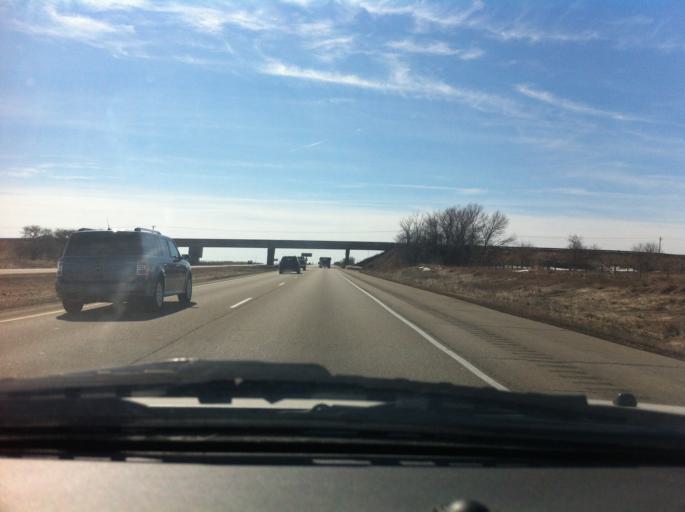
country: US
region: Wisconsin
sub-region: Rock County
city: Janesville
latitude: 42.6677
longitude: -88.9837
